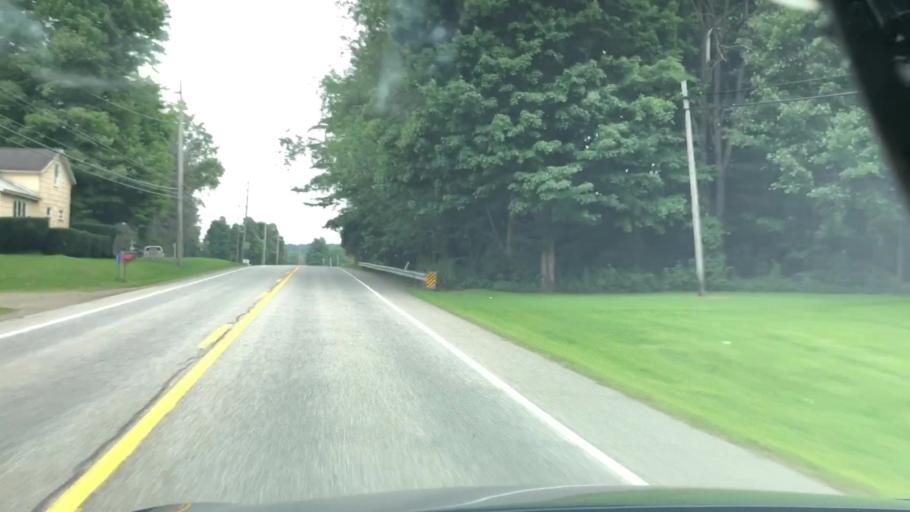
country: US
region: Pennsylvania
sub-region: Erie County
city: Union City
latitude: 42.0110
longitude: -79.8152
